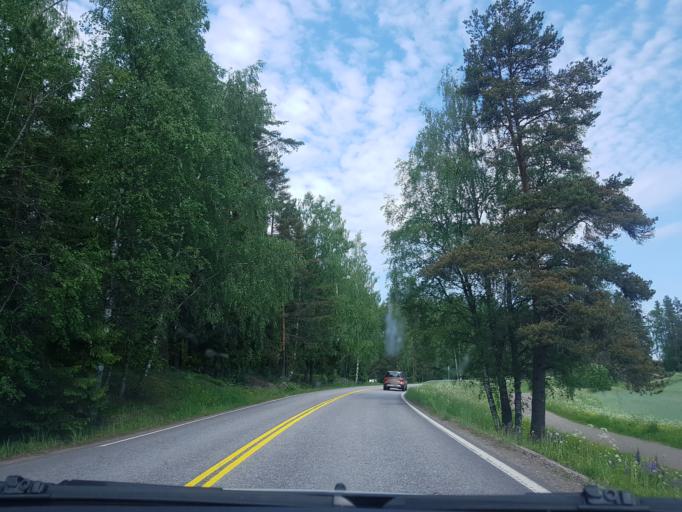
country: FI
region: Uusimaa
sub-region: Helsinki
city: Vihti
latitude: 60.3156
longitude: 24.4040
